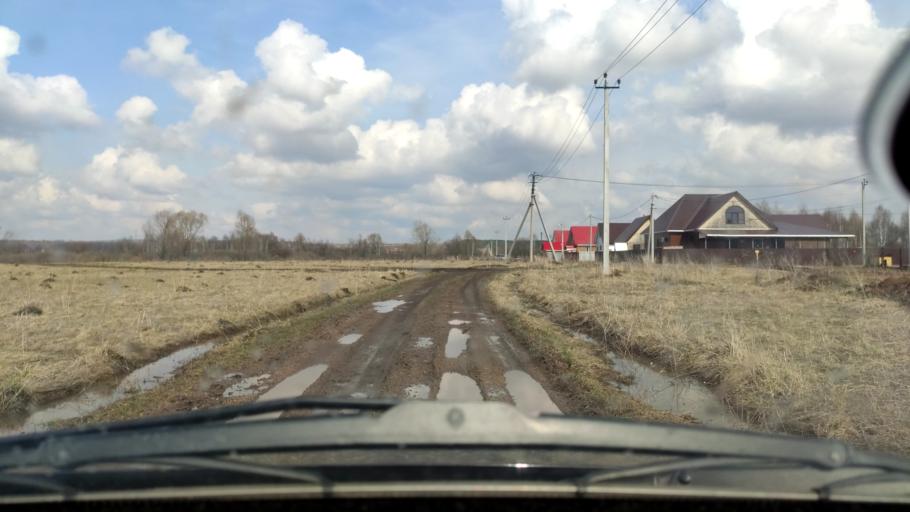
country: RU
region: Bashkortostan
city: Iglino
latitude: 54.8287
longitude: 56.3705
